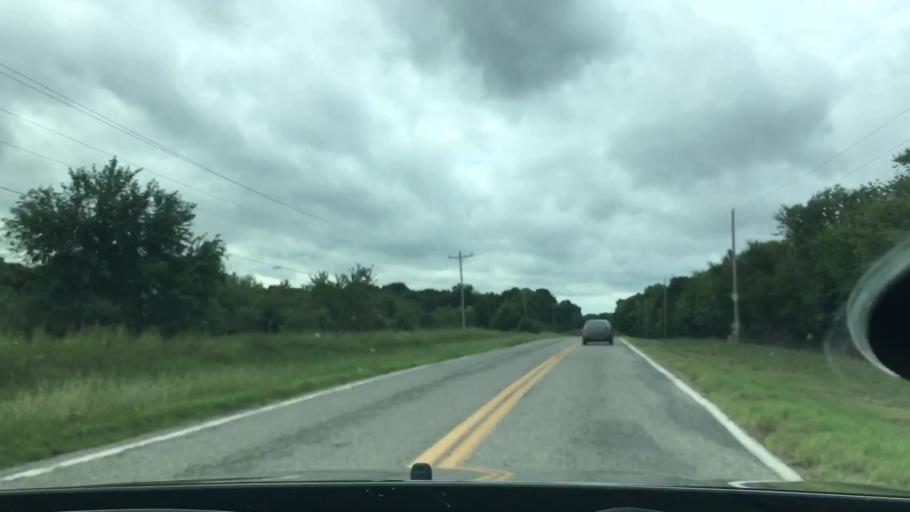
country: US
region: Oklahoma
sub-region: Johnston County
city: Tishomingo
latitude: 34.1754
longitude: -96.5838
